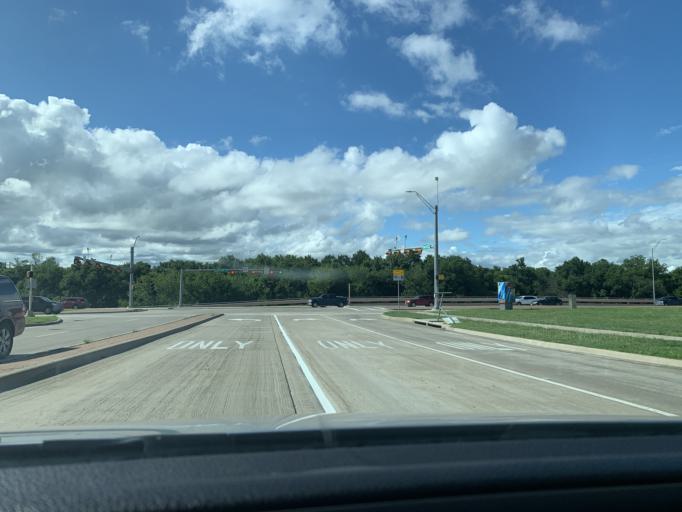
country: US
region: Texas
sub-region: Dallas County
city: Grand Prairie
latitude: 32.6637
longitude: -97.0286
